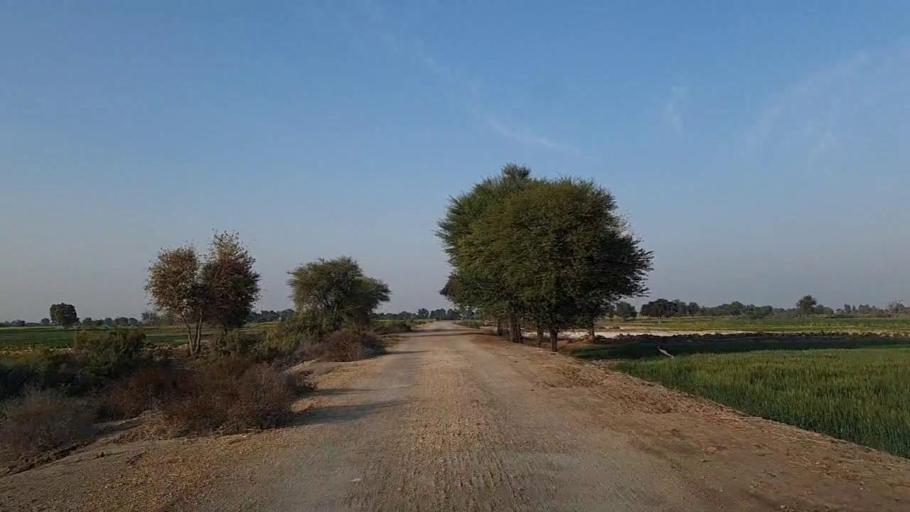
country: PK
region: Sindh
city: Jam Sahib
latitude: 26.3878
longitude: 68.5404
